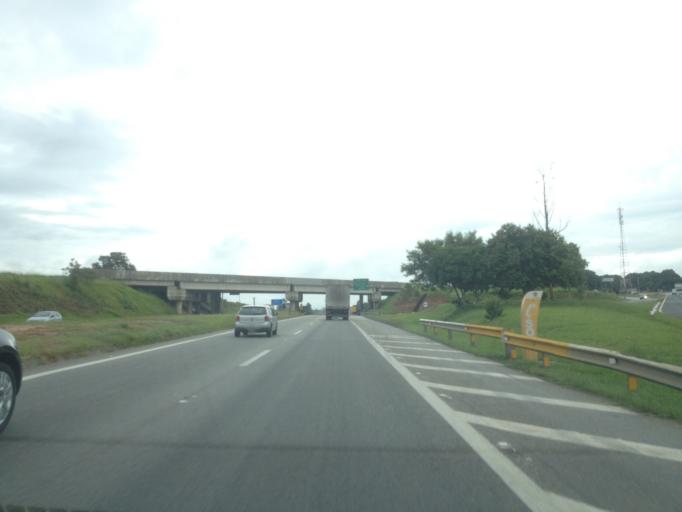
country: BR
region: Sao Paulo
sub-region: Itu
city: Itu
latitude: -23.3771
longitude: -47.3271
